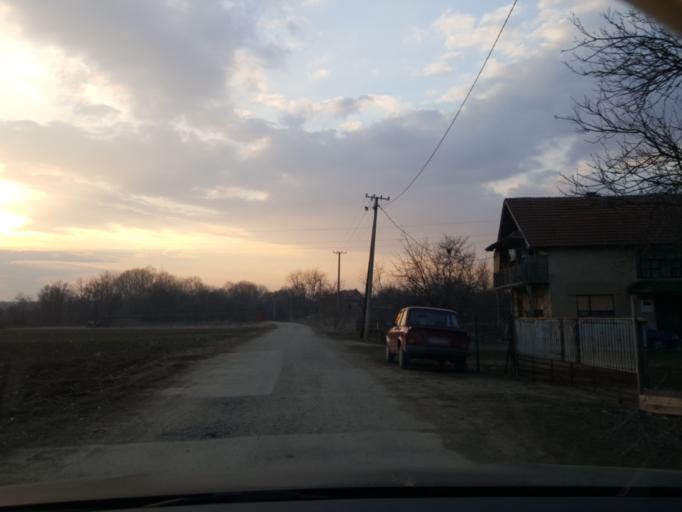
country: RS
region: Central Serbia
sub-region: Nisavski Okrug
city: Aleksinac
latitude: 43.5541
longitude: 21.6563
